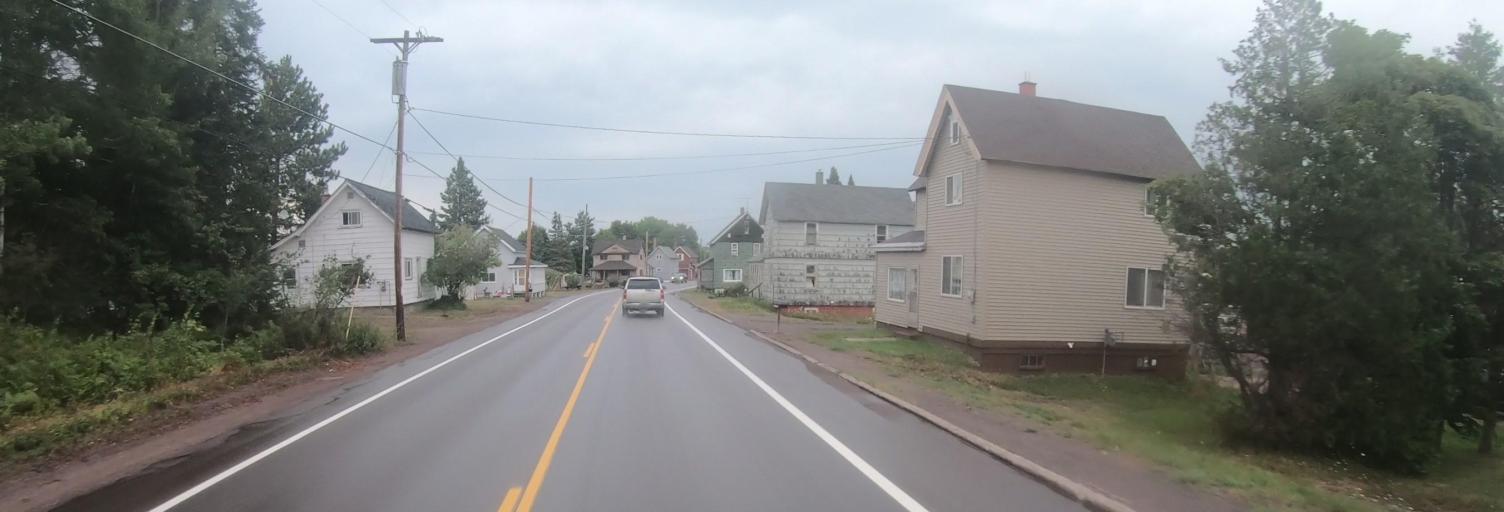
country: US
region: Michigan
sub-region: Houghton County
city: Laurium
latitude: 47.2736
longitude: -88.4175
